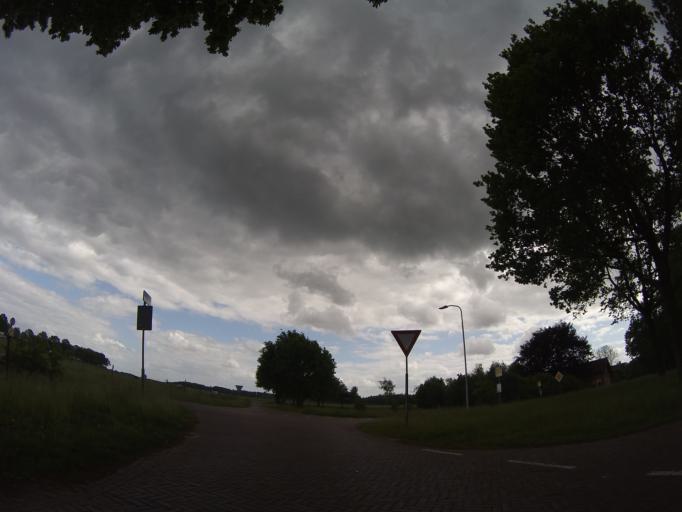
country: NL
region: Drenthe
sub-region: Gemeente Emmen
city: Emmen
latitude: 52.8399
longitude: 6.8735
